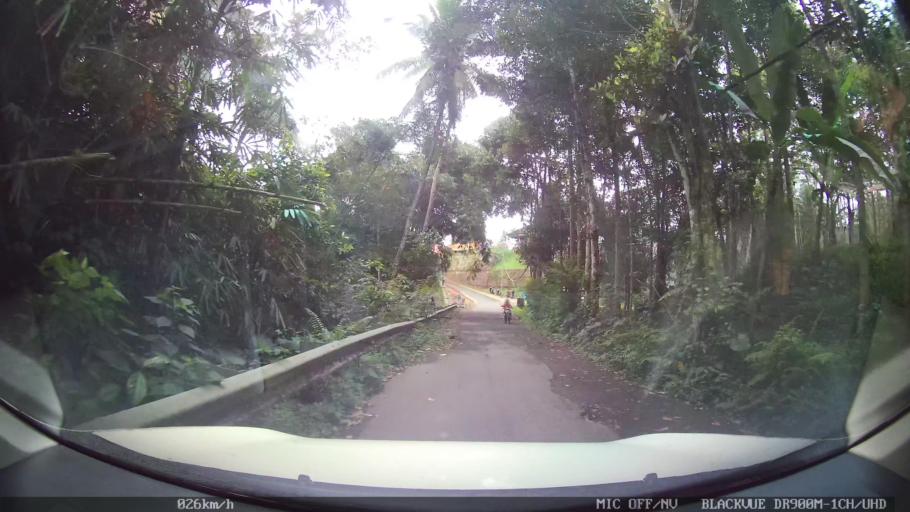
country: ID
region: Bali
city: Banjar Susut Kaja
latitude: -8.4371
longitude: 115.3235
